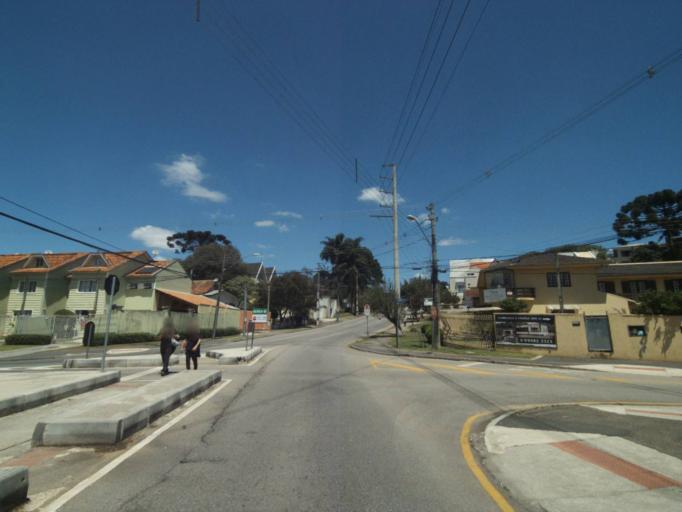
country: BR
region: Parana
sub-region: Curitiba
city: Curitiba
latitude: -25.3943
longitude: -49.2729
